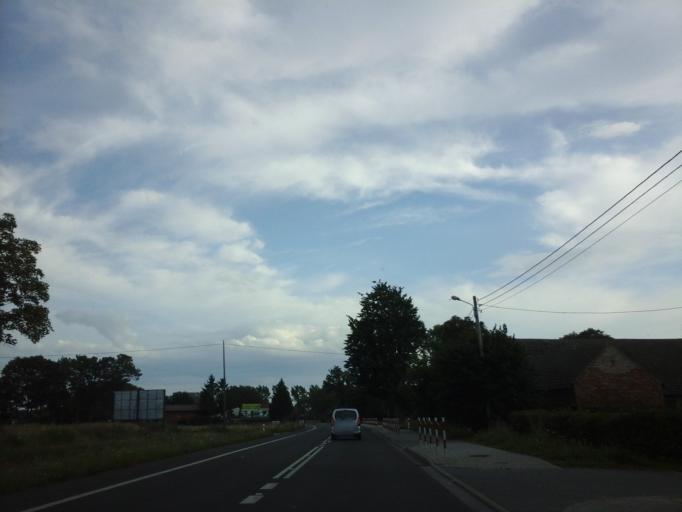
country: PL
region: West Pomeranian Voivodeship
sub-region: Powiat kamienski
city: Dziwnow
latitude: 54.0029
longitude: 14.8169
